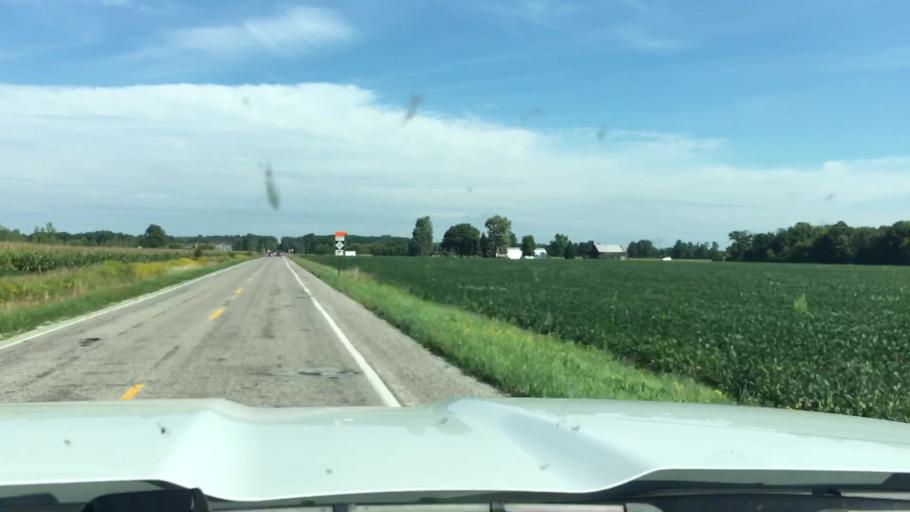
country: US
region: Michigan
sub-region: Saginaw County
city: Hemlock
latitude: 43.4465
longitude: -84.2301
